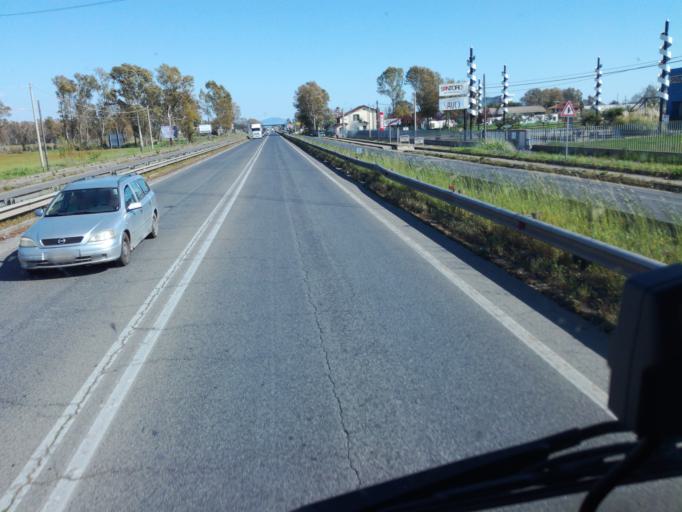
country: IT
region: Latium
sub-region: Provincia di Latina
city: Latina
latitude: 41.4453
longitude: 12.8951
